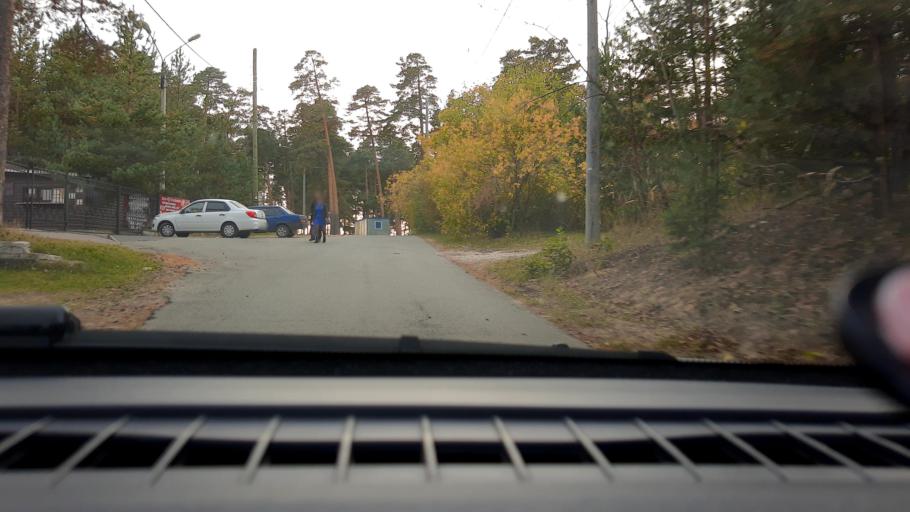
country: RU
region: Nizjnij Novgorod
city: Bor
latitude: 56.3276
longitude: 44.1167
